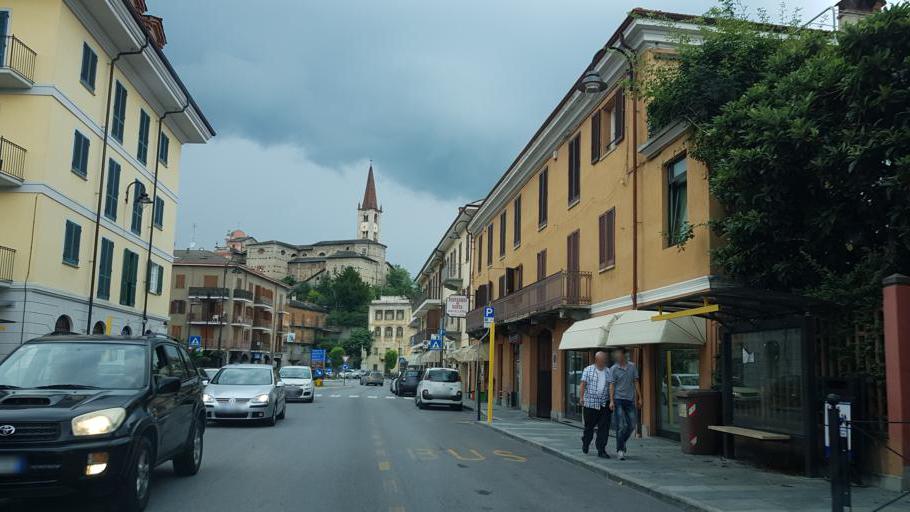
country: IT
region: Piedmont
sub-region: Provincia di Cuneo
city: Caraglio
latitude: 44.4185
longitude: 7.4332
